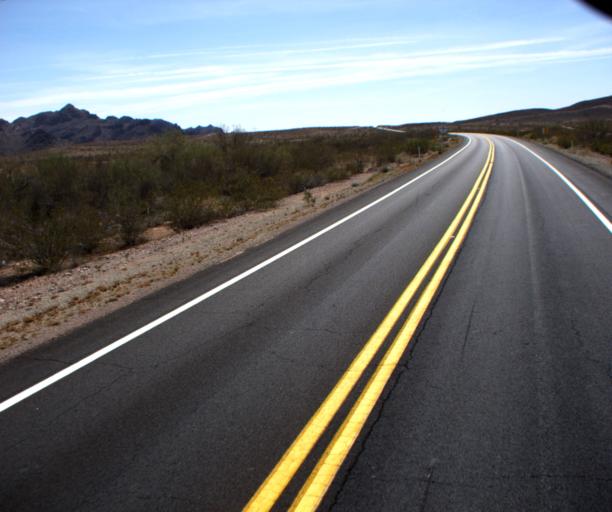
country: US
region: Arizona
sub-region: La Paz County
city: Quartzsite
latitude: 33.2559
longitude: -114.2455
